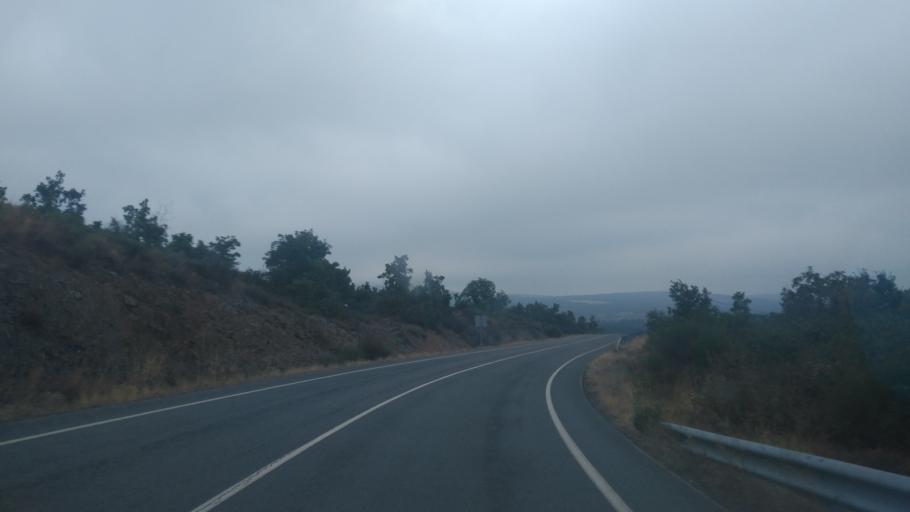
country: ES
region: Castille and Leon
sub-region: Provincia de Salamanca
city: Cilleros de la Bastida
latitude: 40.5791
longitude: -6.0782
